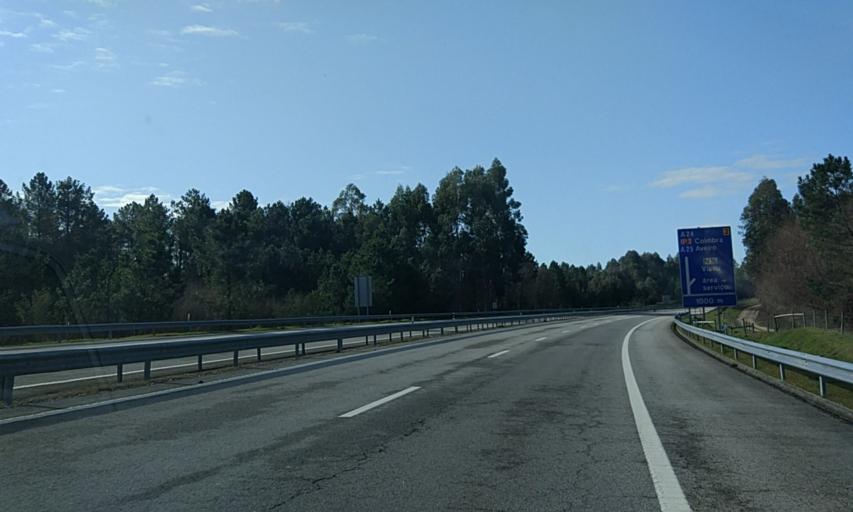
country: PT
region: Viseu
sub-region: Viseu
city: Campo
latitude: 40.7168
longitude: -7.9298
